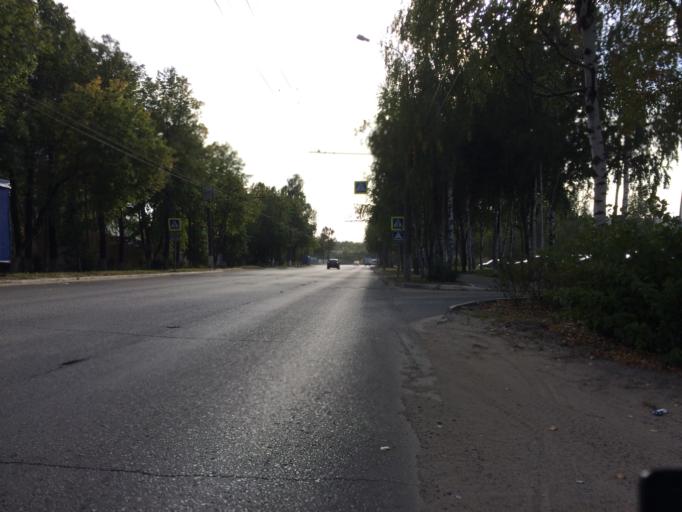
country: RU
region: Mariy-El
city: Medvedevo
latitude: 56.6268
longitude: 47.8408
